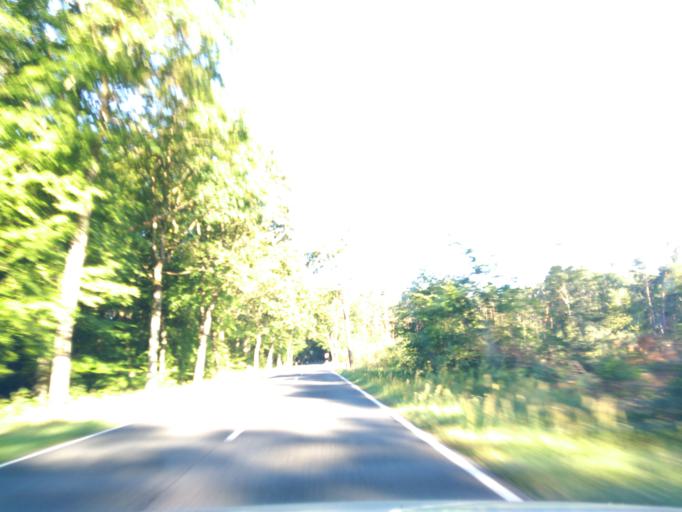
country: DE
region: Brandenburg
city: Brieselang
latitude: 52.6176
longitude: 12.9938
